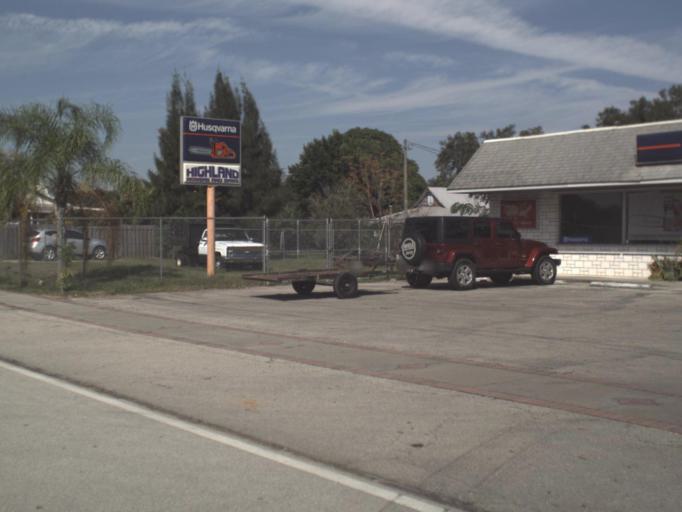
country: US
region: Florida
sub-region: Highlands County
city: Avon Park
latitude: 27.5959
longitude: -81.5109
